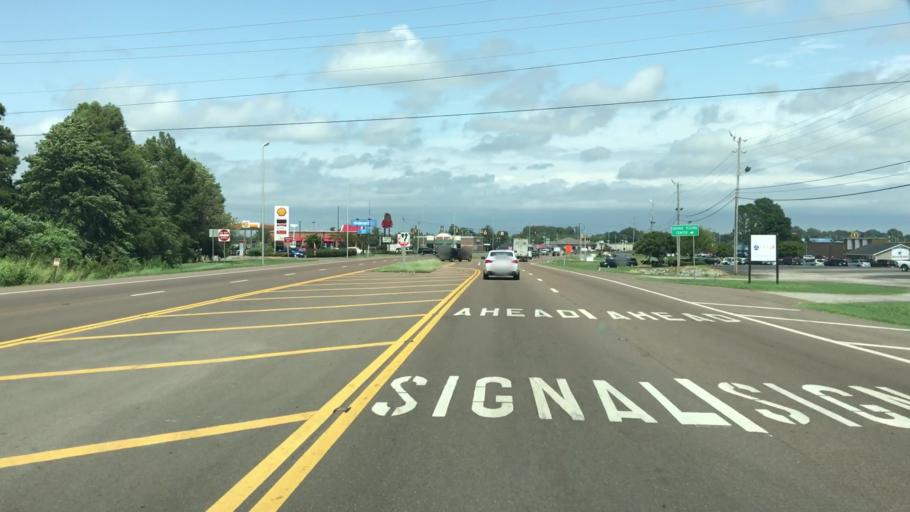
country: US
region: Tennessee
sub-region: Obion County
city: Union City
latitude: 36.4122
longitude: -89.0782
